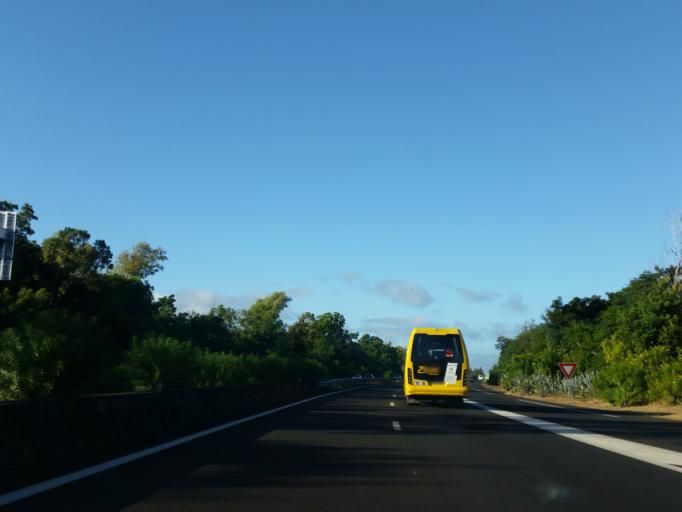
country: RE
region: Reunion
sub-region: Reunion
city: Les Avirons
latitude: -21.2655
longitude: 55.3397
